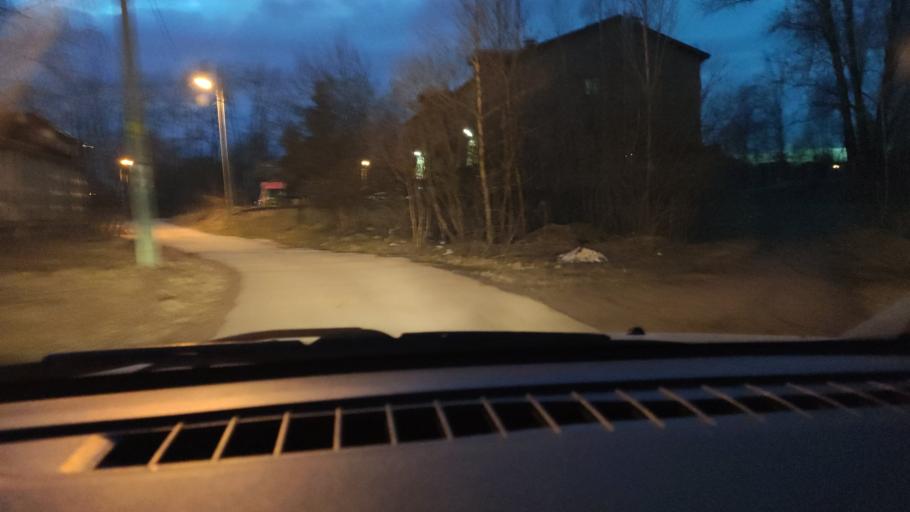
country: RU
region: Perm
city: Perm
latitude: 58.0464
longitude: 56.2862
